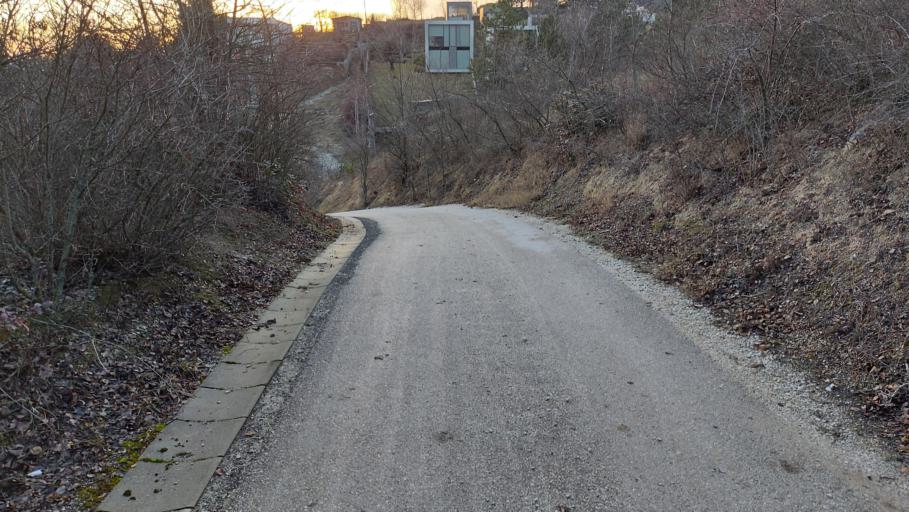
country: HU
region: Pest
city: Toeroekbalint
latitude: 47.4614
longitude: 18.9142
